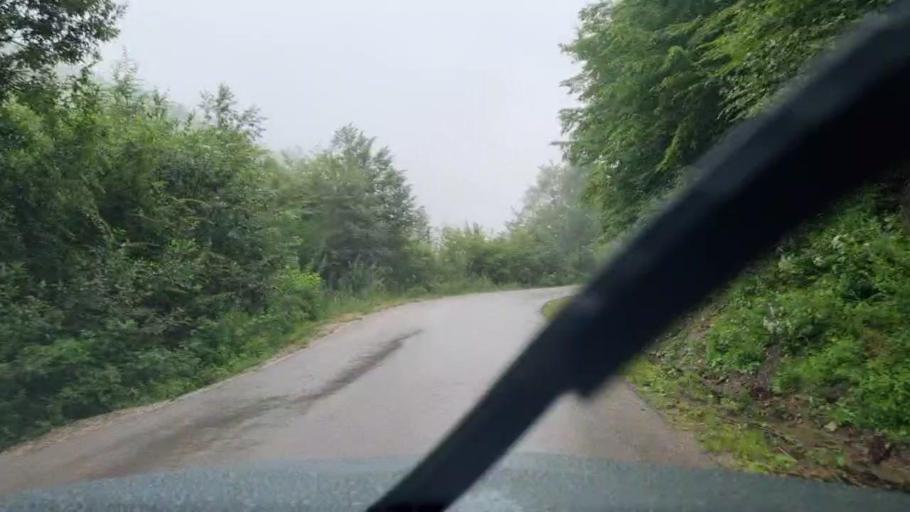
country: BA
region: Federation of Bosnia and Herzegovina
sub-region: Bosansko-Podrinjski Kanton
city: Ustikolina
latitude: 43.6331
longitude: 18.6322
